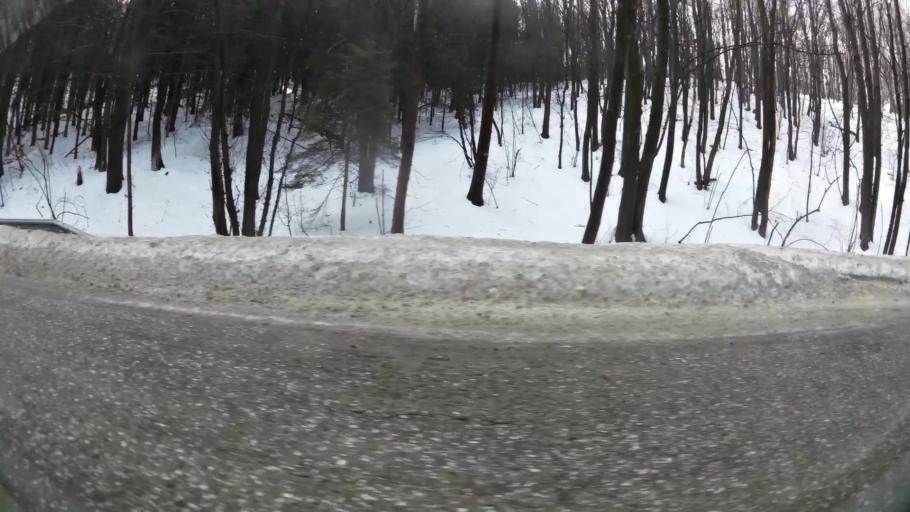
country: BG
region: Sofiya
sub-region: Obshtina Bozhurishte
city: Bozhurishte
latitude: 42.6408
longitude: 23.2201
